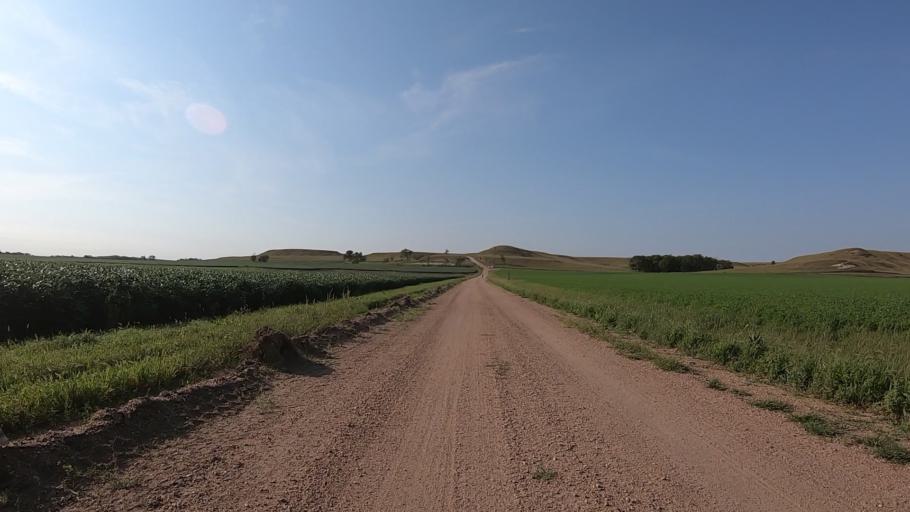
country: US
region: Kansas
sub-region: Marshall County
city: Blue Rapids
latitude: 39.6544
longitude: -96.8815
